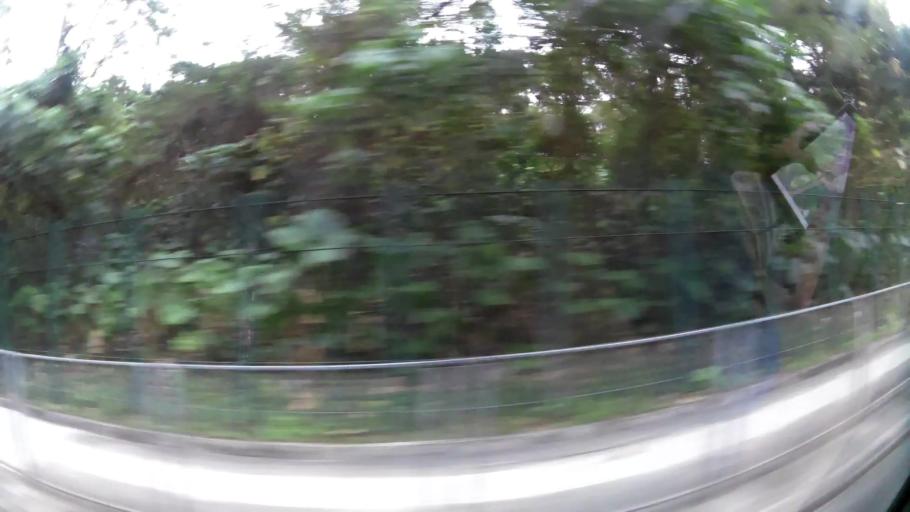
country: HK
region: Tsuen Wan
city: Tsuen Wan
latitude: 22.3557
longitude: 114.1181
